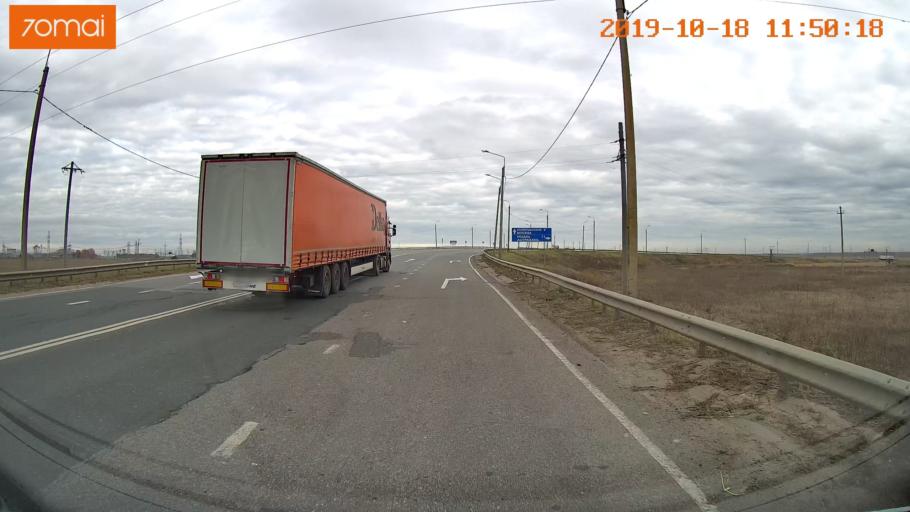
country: RU
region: Rjazan
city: Mikhaylov
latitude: 54.2598
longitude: 39.0023
